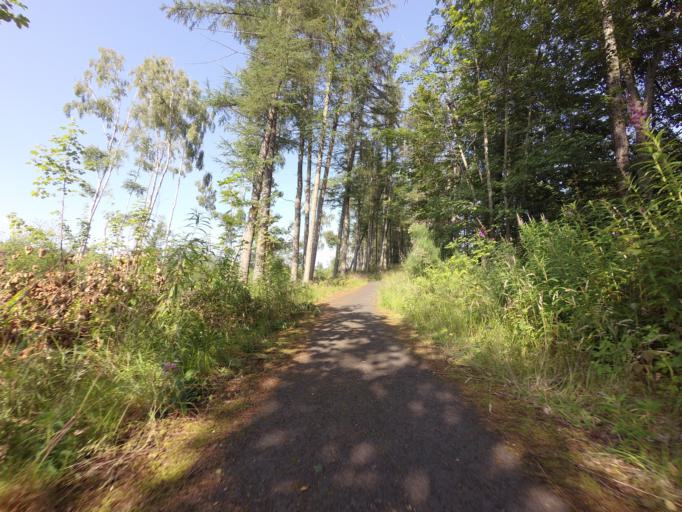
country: GB
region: Scotland
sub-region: Highland
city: Evanton
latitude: 57.6795
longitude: -4.3023
